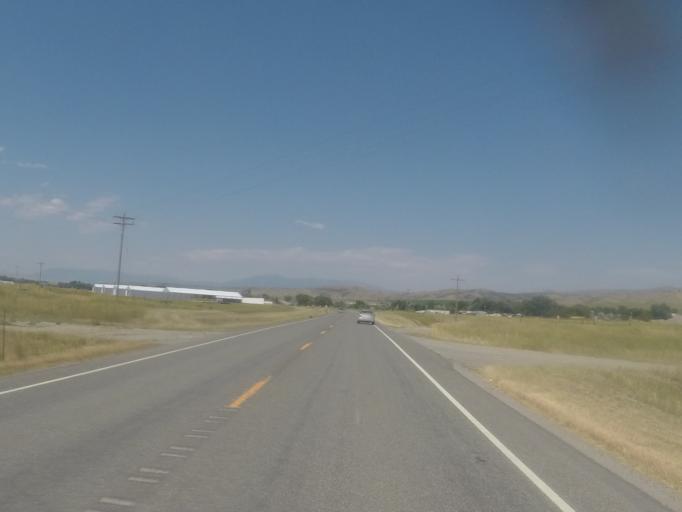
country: US
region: Montana
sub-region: Broadwater County
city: Townsend
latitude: 46.1668
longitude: -111.4515
